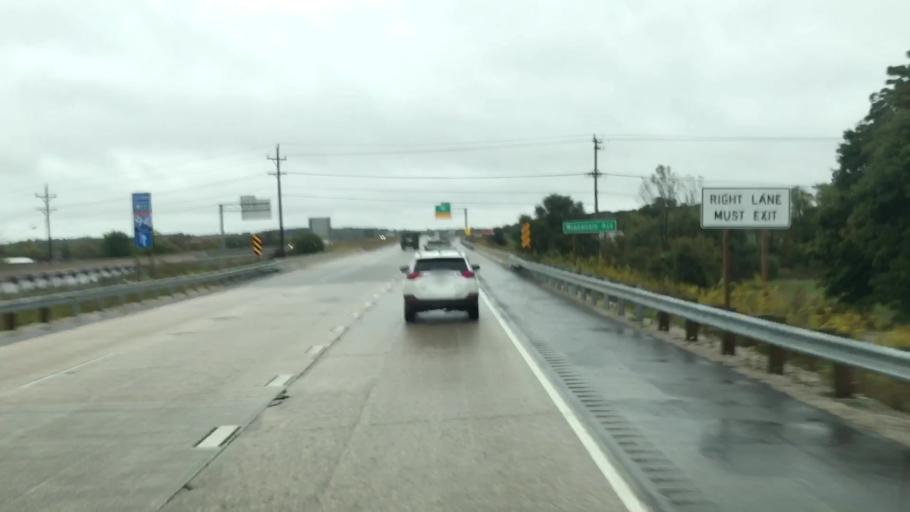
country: US
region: Wisconsin
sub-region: Waukesha County
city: Pewaukee
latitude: 43.0777
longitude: -88.2512
